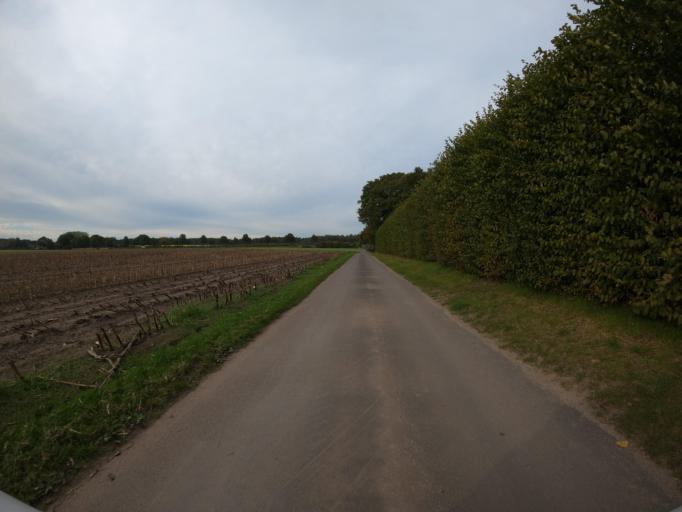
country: DE
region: North Rhine-Westphalia
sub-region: Regierungsbezirk Dusseldorf
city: Schermbeck
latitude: 51.6954
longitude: 6.8987
